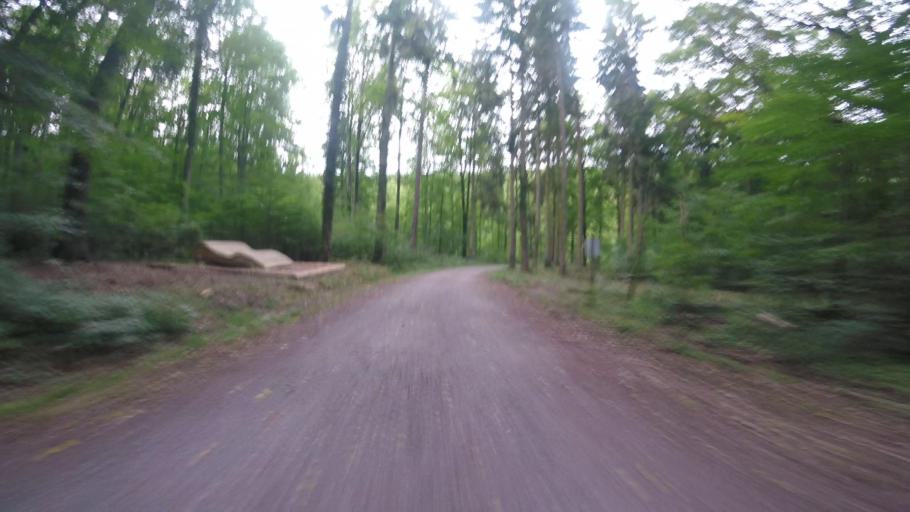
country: DE
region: Baden-Wuerttemberg
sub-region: Regierungsbezirk Stuttgart
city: Grossbottwar
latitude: 48.9913
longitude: 9.3270
